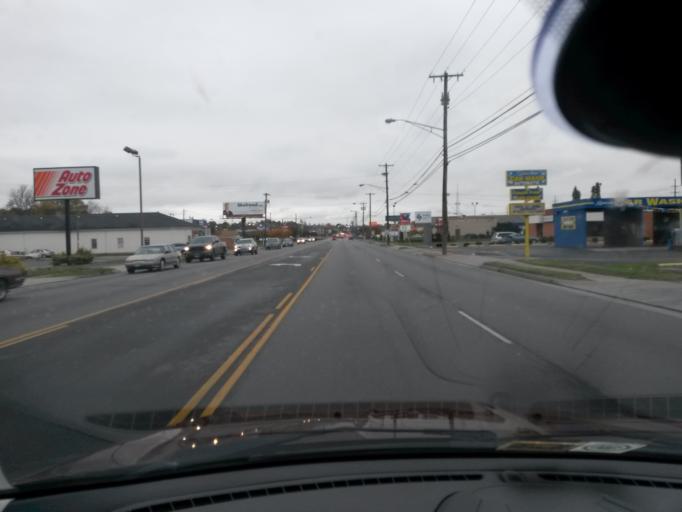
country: US
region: Virginia
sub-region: City of Salem
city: Salem
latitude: 37.2888
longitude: -80.0864
